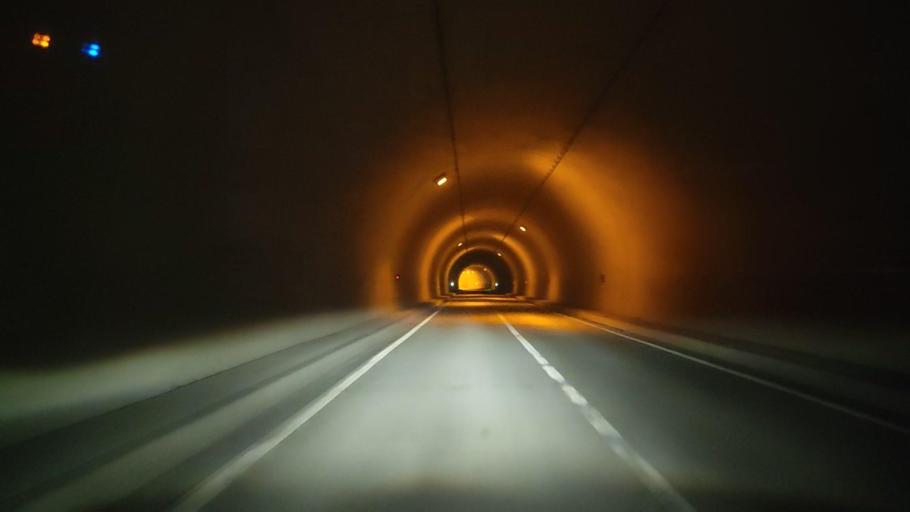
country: JP
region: Kumamoto
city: Matsubase
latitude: 32.5056
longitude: 130.9181
